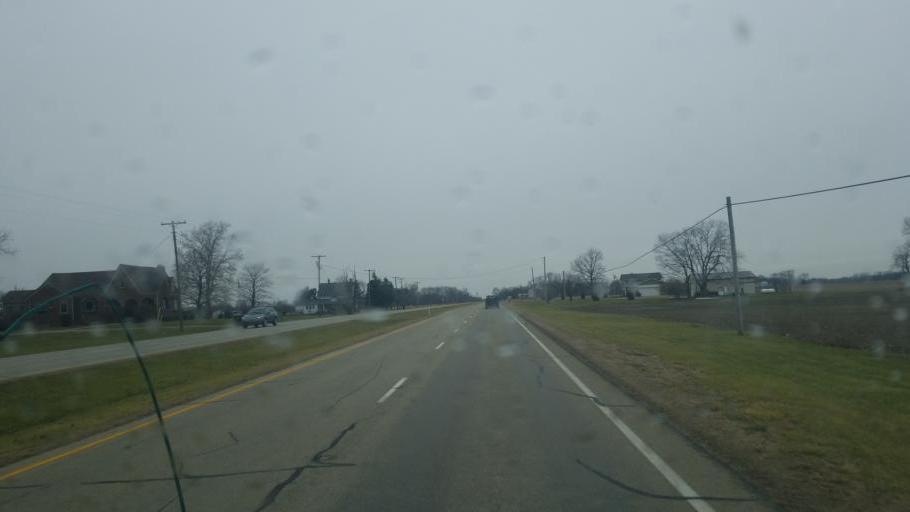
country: US
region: Indiana
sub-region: Henry County
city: Knightstown
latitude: 39.7909
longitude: -85.6334
